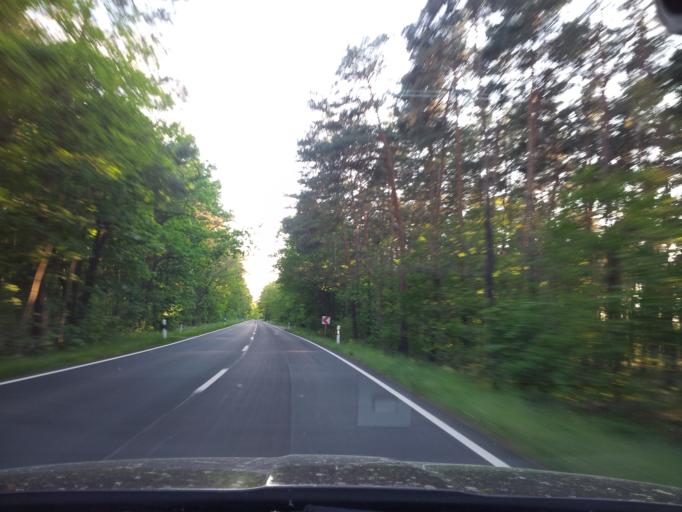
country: DE
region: Brandenburg
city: Luckenwalde
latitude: 52.0532
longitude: 13.1409
